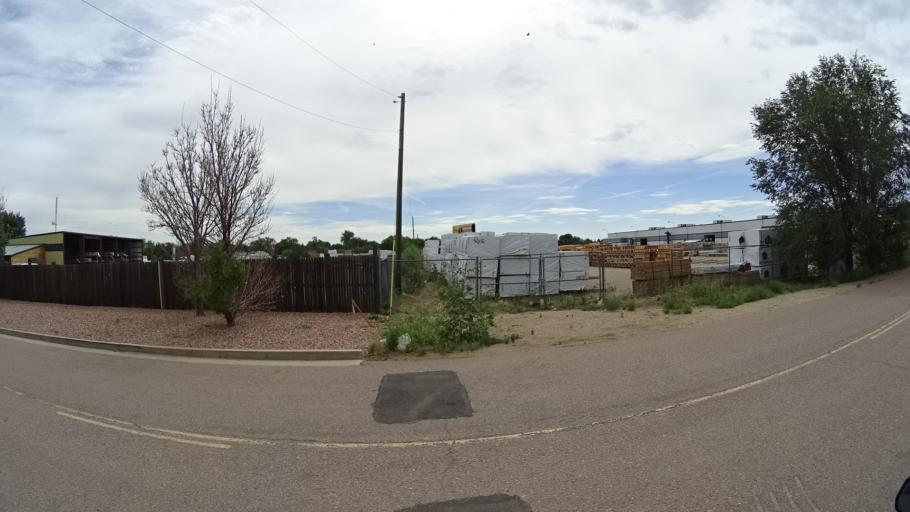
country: US
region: Colorado
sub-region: El Paso County
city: Fountain
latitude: 38.6773
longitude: -104.7151
